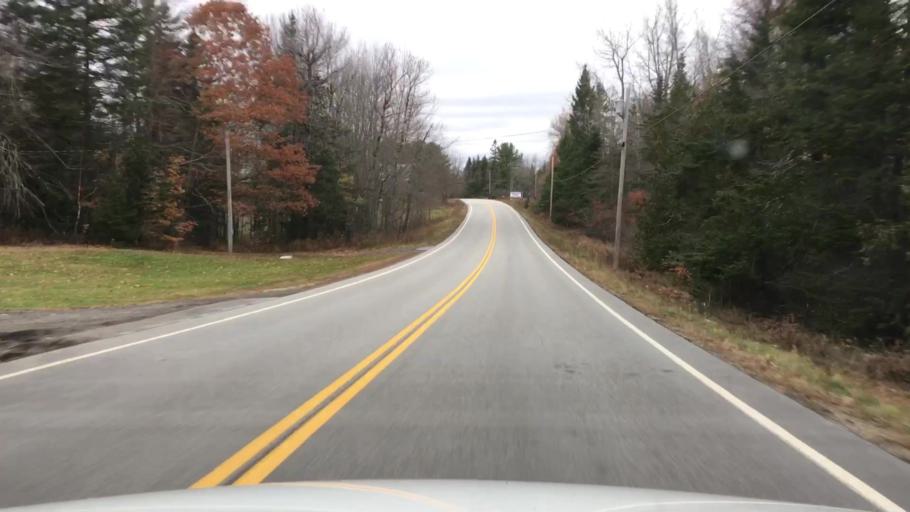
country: US
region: Maine
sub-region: Hancock County
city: Penobscot
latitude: 44.4925
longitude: -68.6441
